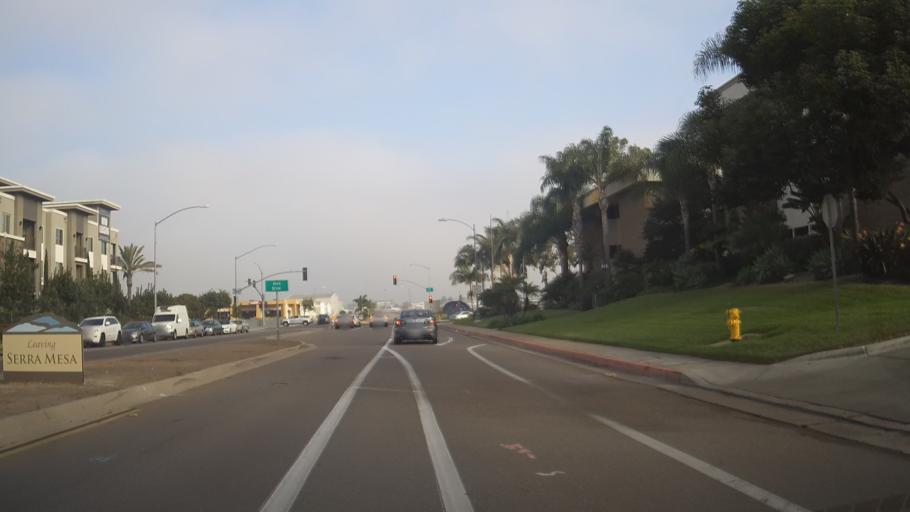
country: US
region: California
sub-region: San Diego County
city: San Diego
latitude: 32.8086
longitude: -117.1401
